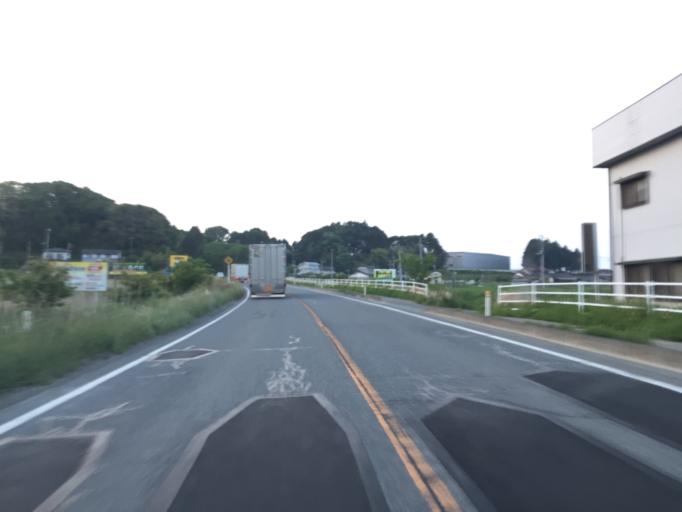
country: JP
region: Fukushima
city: Namie
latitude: 37.6074
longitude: 141.0070
